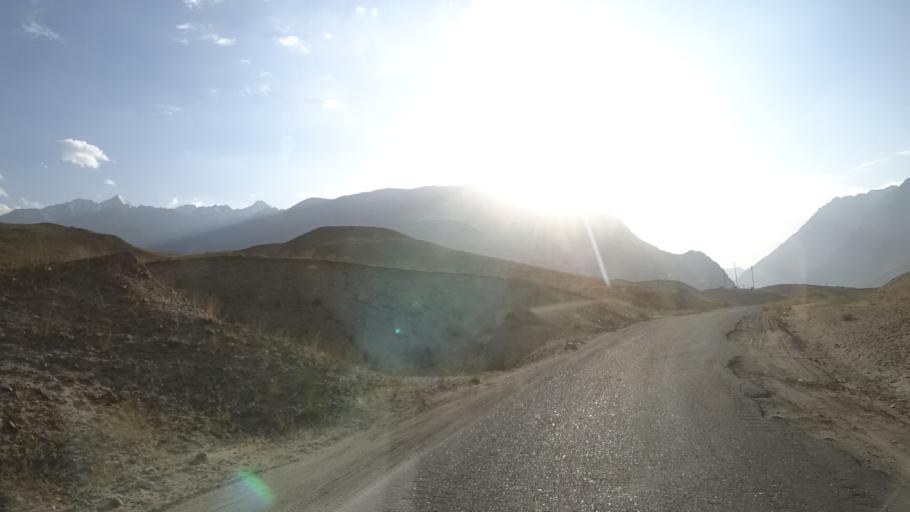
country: TJ
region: Gorno-Badakhshan
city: Vanj
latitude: 38.2900
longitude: 71.3452
